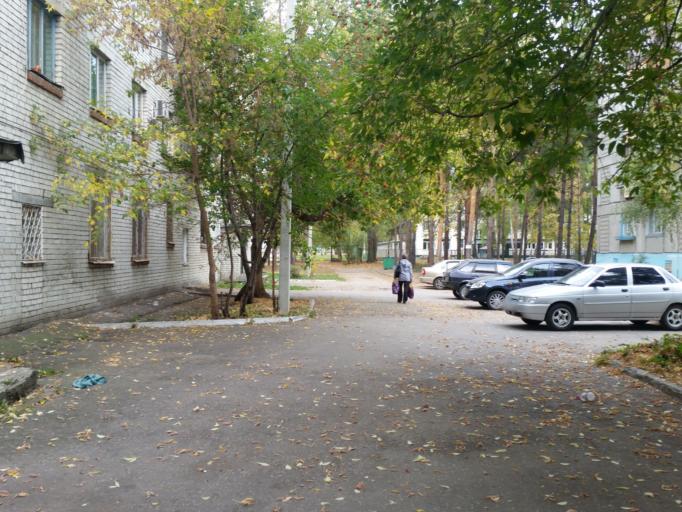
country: RU
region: Ulyanovsk
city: Dimitrovgrad
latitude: 54.2108
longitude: 49.5925
